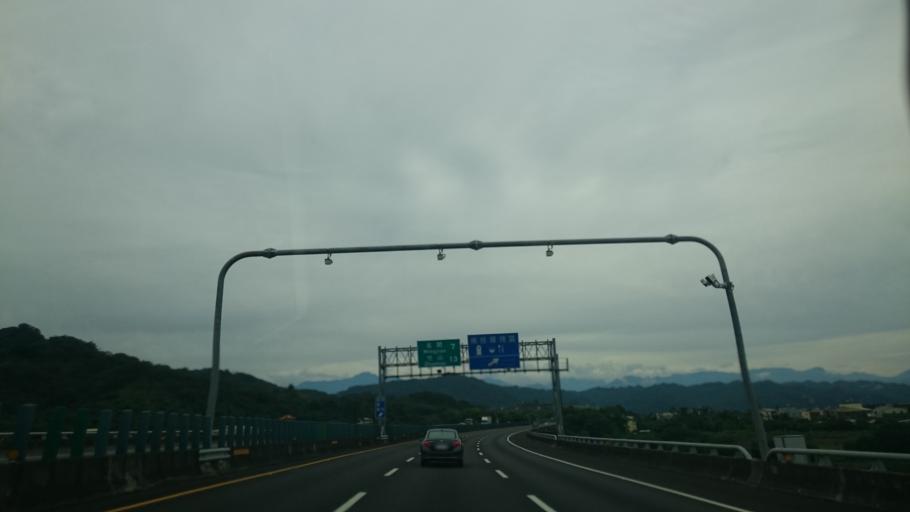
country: TW
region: Taiwan
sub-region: Nantou
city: Nantou
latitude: 23.9092
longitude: 120.7010
